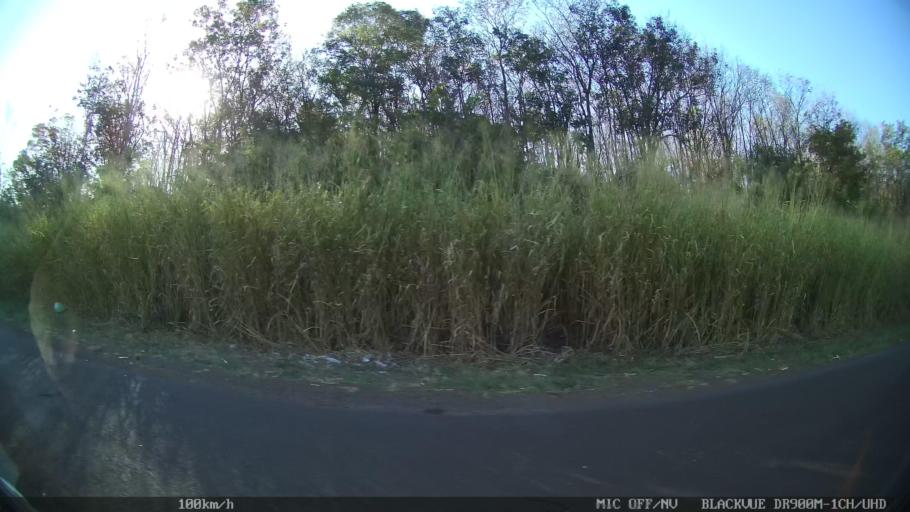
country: BR
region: Sao Paulo
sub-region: Guapiacu
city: Guapiacu
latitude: -20.7656
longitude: -49.1958
